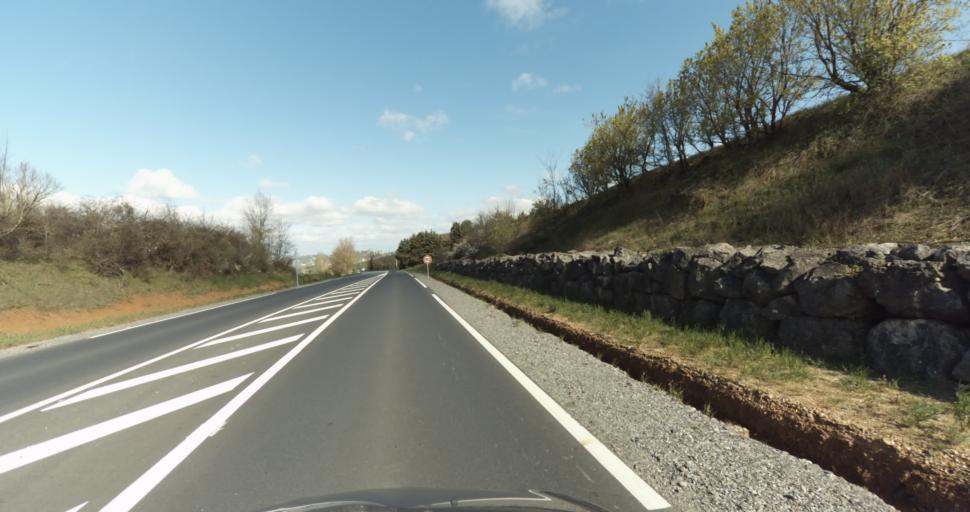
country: FR
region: Midi-Pyrenees
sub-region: Departement du Tarn
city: Puygouzon
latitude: 43.8661
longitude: 2.1866
